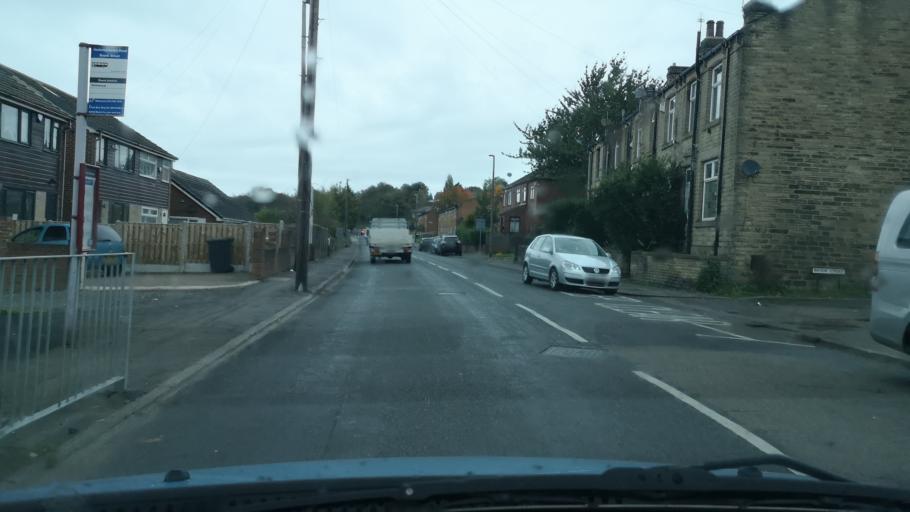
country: GB
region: England
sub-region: Kirklees
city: Heckmondwike
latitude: 53.6938
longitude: -1.6570
